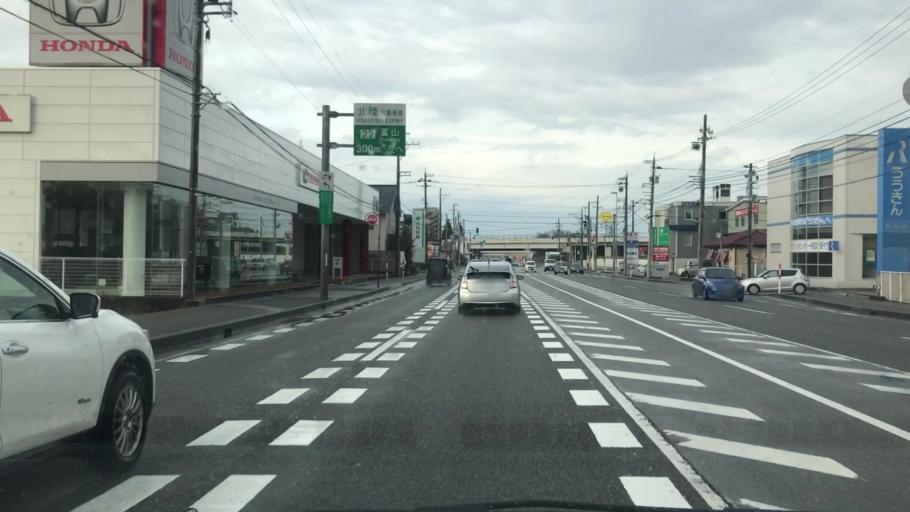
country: JP
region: Toyama
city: Toyama-shi
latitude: 36.6504
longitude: 137.2096
